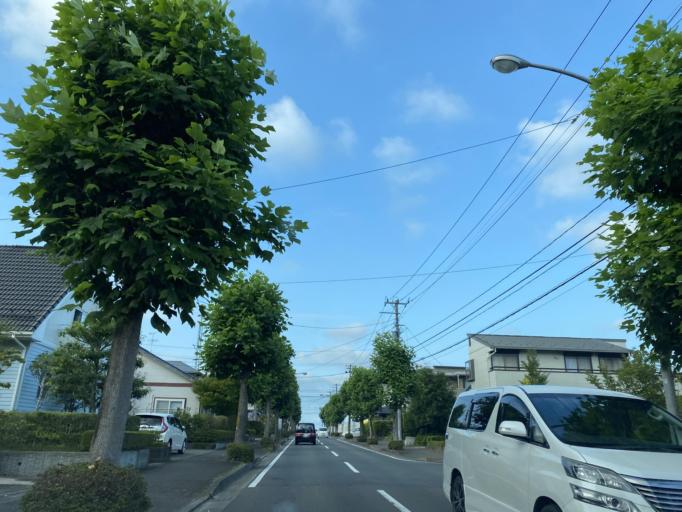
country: JP
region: Miyagi
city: Tomiya
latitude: 38.3812
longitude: 140.8656
